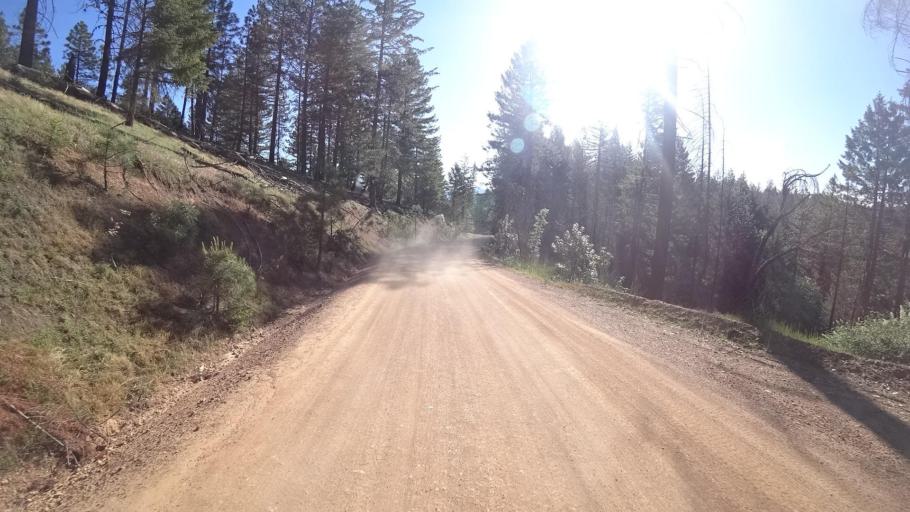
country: US
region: California
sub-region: Lake County
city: Upper Lake
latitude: 39.3576
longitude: -122.9872
